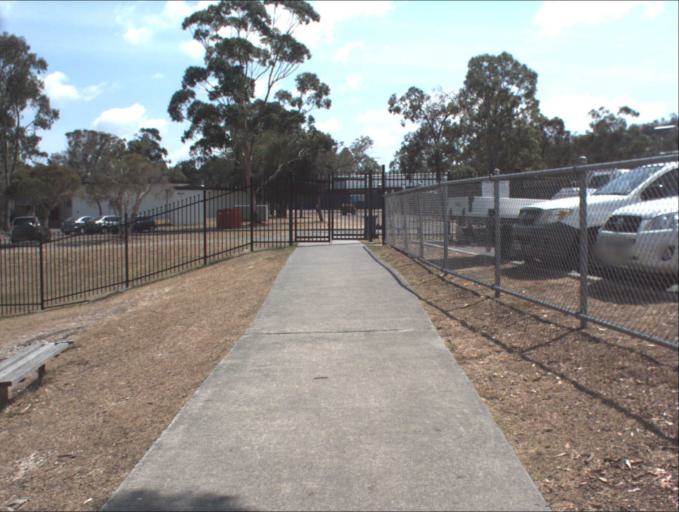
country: AU
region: Queensland
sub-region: Logan
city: Slacks Creek
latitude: -27.6643
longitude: 153.1873
